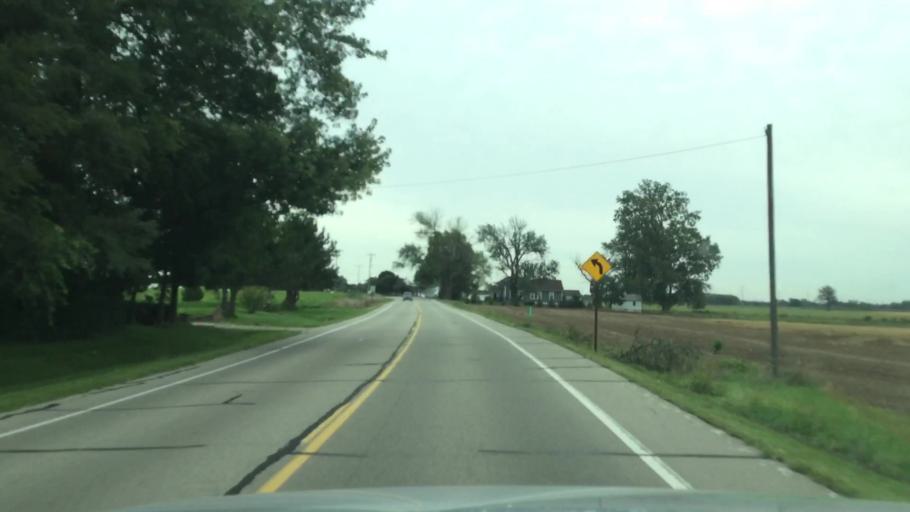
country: US
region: Michigan
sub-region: Washtenaw County
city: Milan
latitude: 42.1151
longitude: -83.7127
